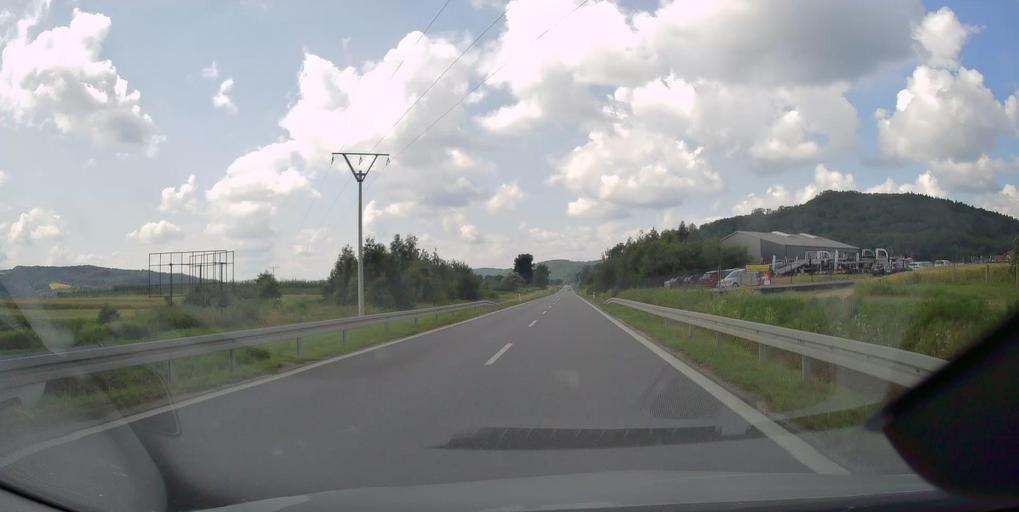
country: PL
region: Lesser Poland Voivodeship
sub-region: Powiat tarnowski
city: Wielka Wies
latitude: 49.9296
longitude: 20.8415
